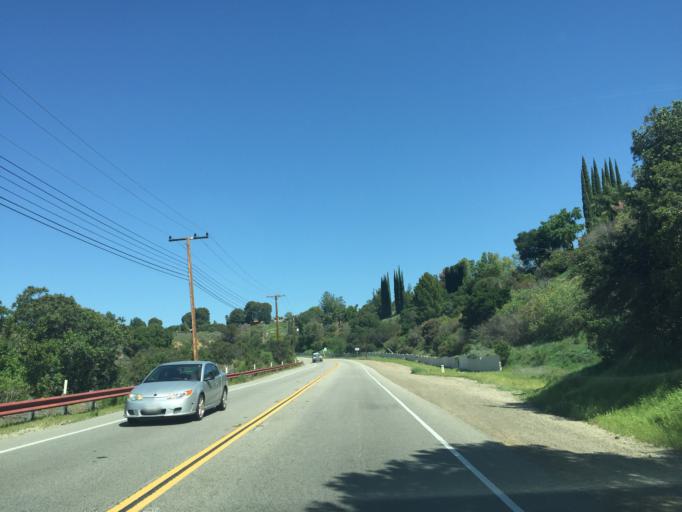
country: US
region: California
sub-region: Los Angeles County
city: Woodland Hills
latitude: 34.1326
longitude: -118.5992
